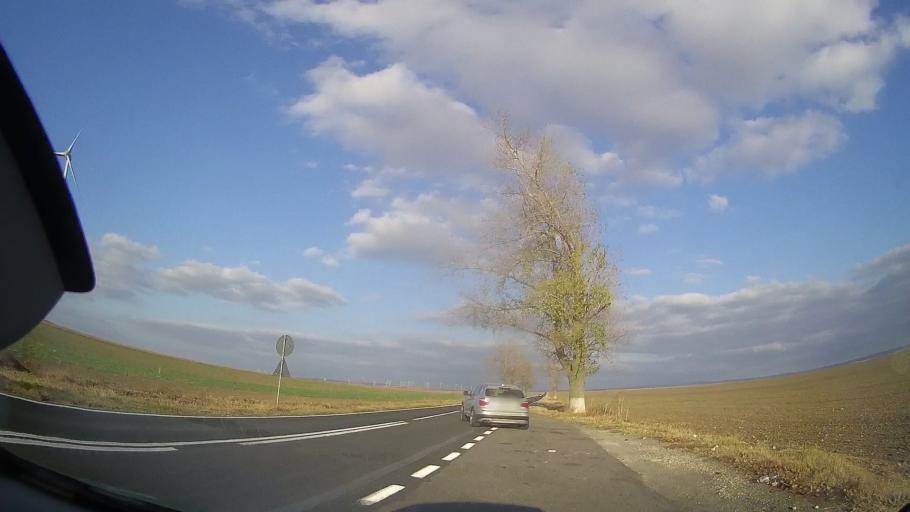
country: RO
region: Tulcea
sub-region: Comuna Topolog
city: Topolog
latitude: 44.8259
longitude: 28.2745
